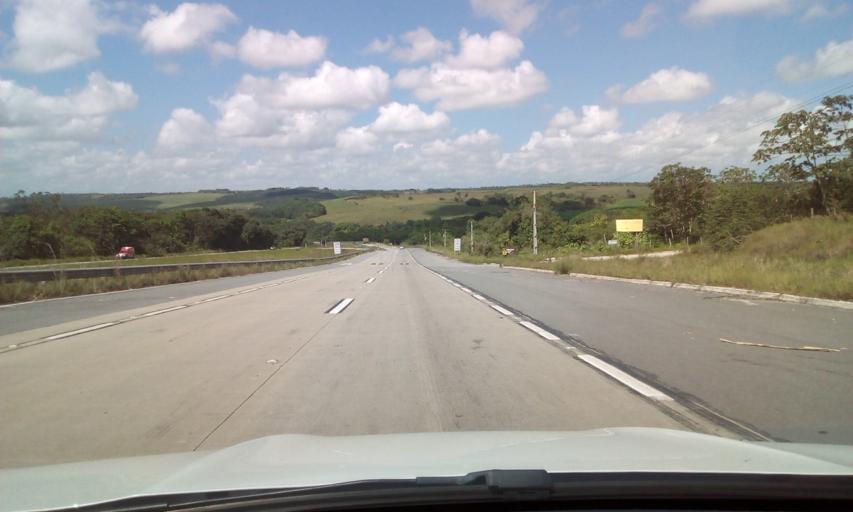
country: BR
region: Paraiba
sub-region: Alhandra
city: Alhandra
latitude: -7.4143
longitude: -34.9574
